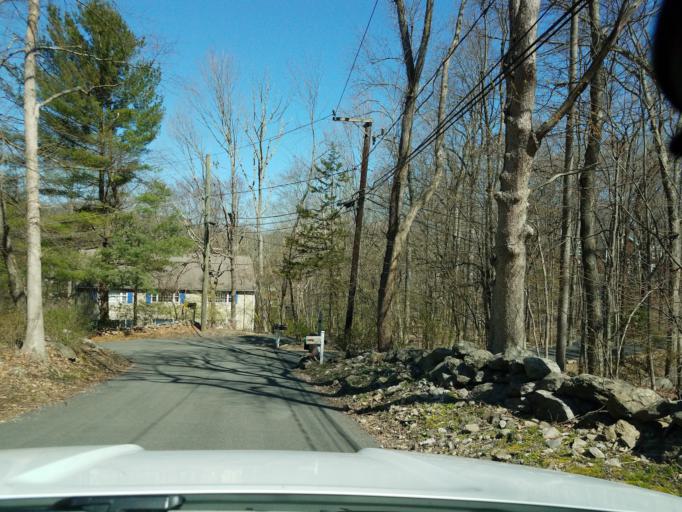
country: US
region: Connecticut
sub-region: Fairfield County
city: Wilton
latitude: 41.2215
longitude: -73.3806
